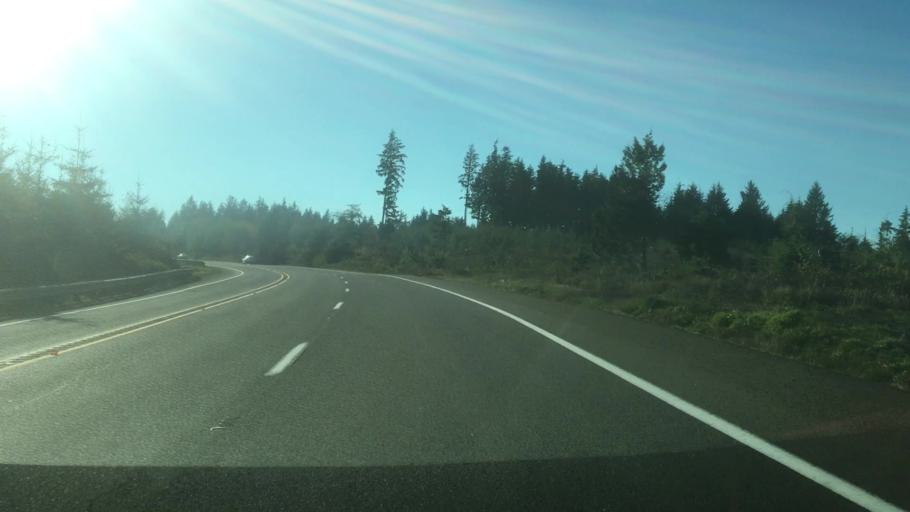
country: US
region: Washington
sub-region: Pacific County
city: South Bend
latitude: 46.6856
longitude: -123.8847
